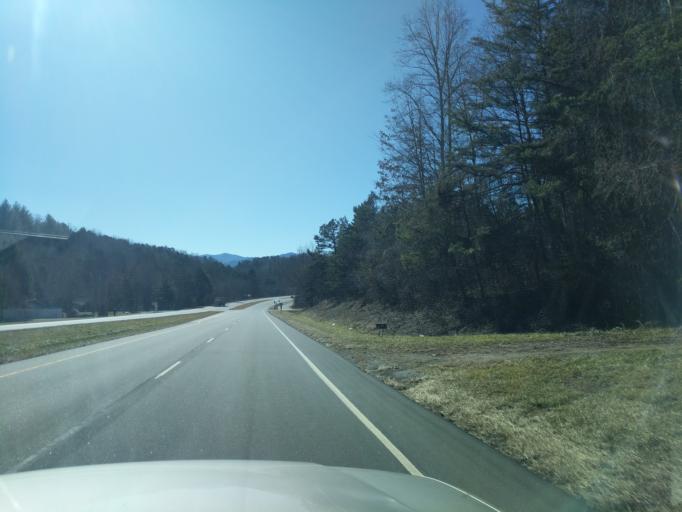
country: US
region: North Carolina
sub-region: Swain County
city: Bryson City
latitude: 35.3771
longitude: -83.5002
